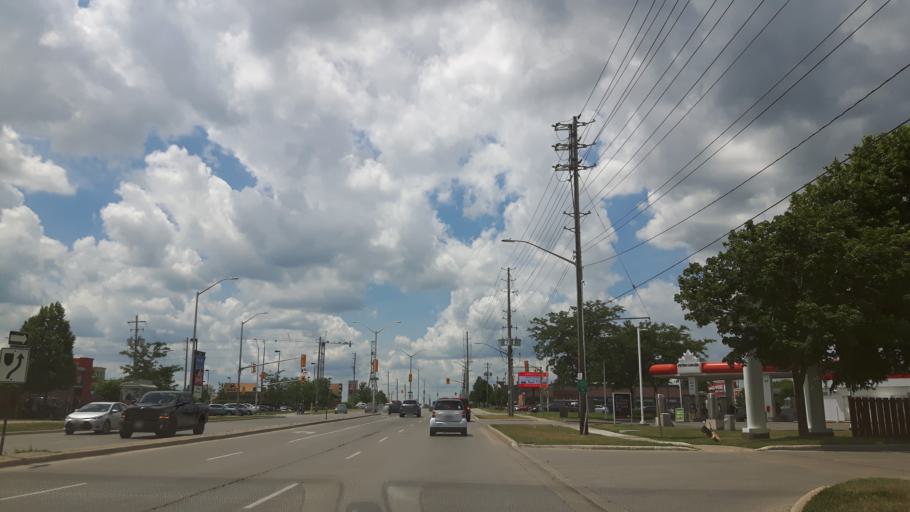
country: CA
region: Ontario
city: London
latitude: 42.9391
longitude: -81.2800
